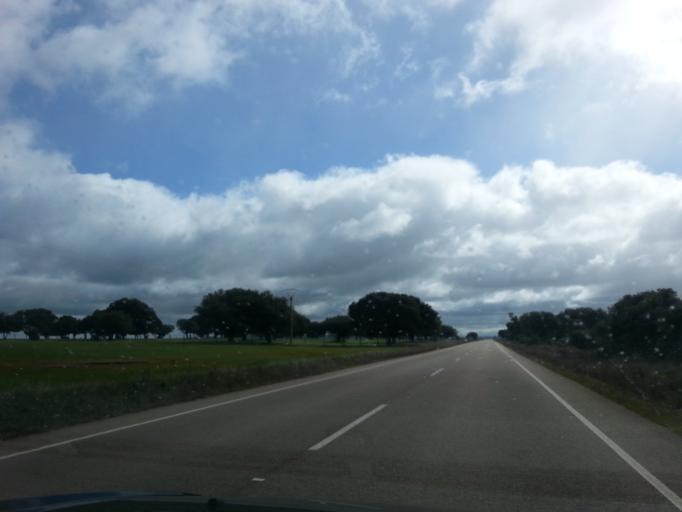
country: ES
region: Castille and Leon
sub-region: Provincia de Salamanca
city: Cabrillas
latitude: 40.7582
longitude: -6.1958
